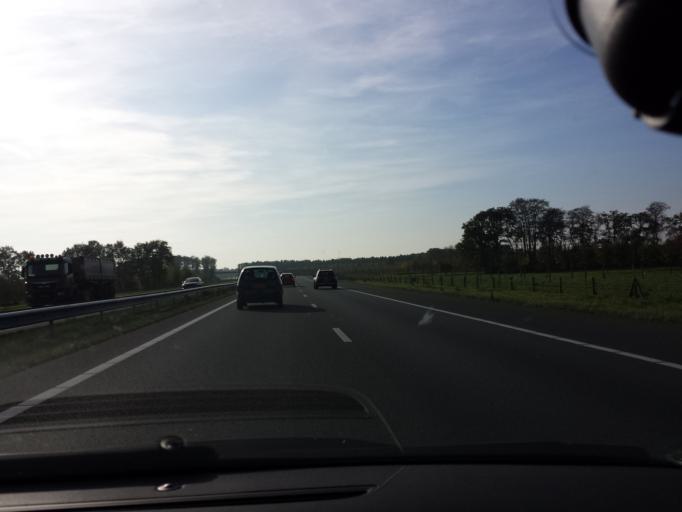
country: NL
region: Limburg
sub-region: Gemeente Beesel
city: Offenbeek
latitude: 51.2976
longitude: 6.1096
